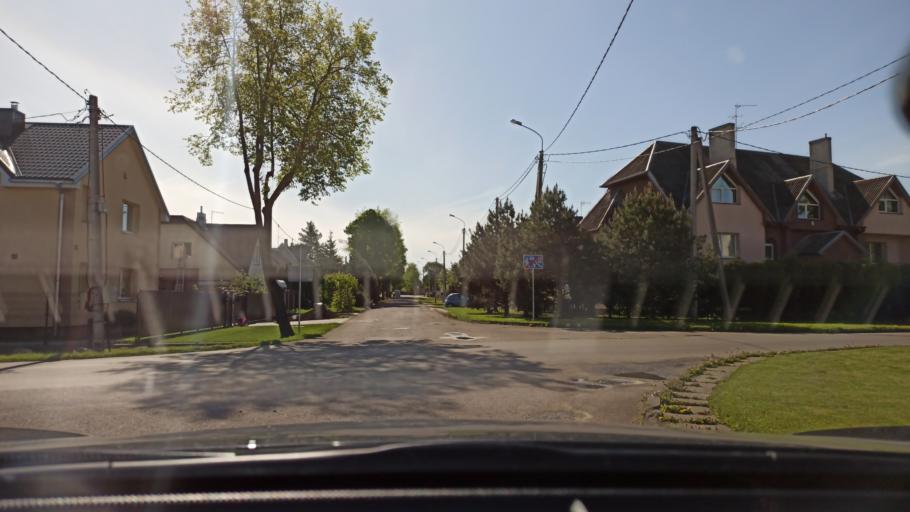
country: LT
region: Siauliu apskritis
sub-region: Siauliai
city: Siauliai
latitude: 55.9464
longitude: 23.3082
